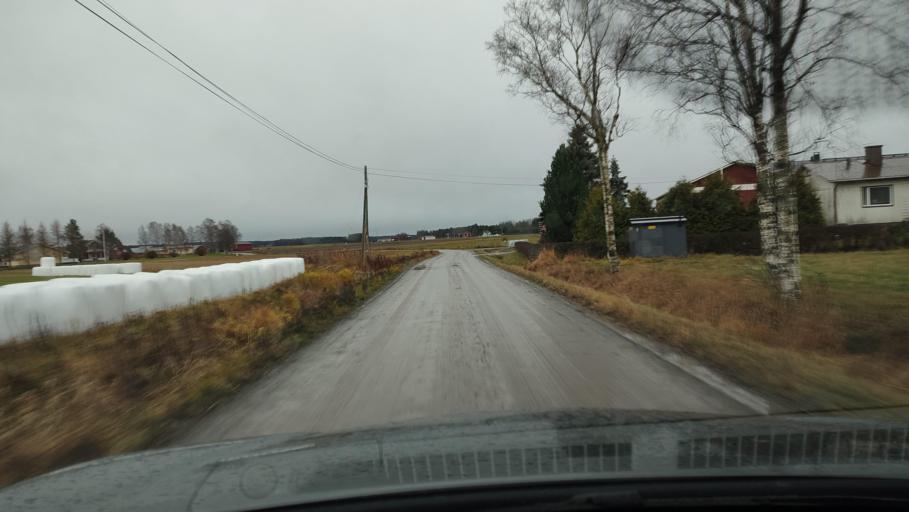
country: FI
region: Southern Ostrobothnia
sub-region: Suupohja
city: Karijoki
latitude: 62.2463
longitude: 21.5486
